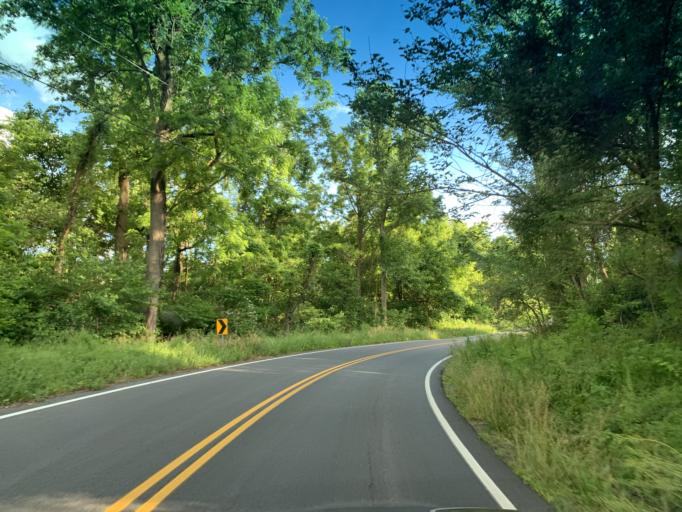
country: US
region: Maryland
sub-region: Cecil County
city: Rising Sun
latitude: 39.6308
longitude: -76.0528
